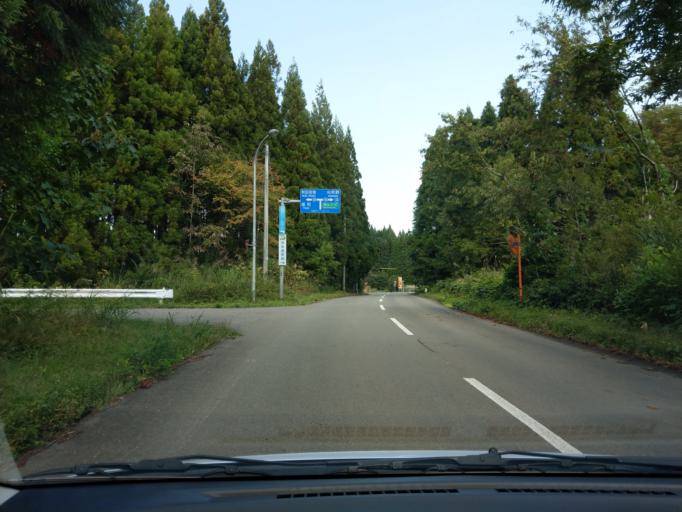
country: JP
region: Akita
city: Omagari
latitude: 39.5221
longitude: 140.2961
